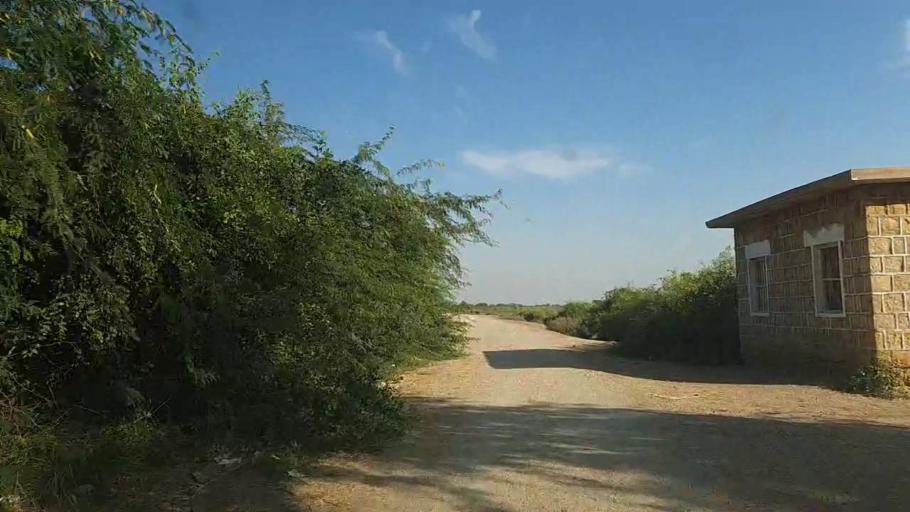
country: PK
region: Sindh
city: Mirpur Batoro
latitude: 24.7616
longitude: 68.3582
